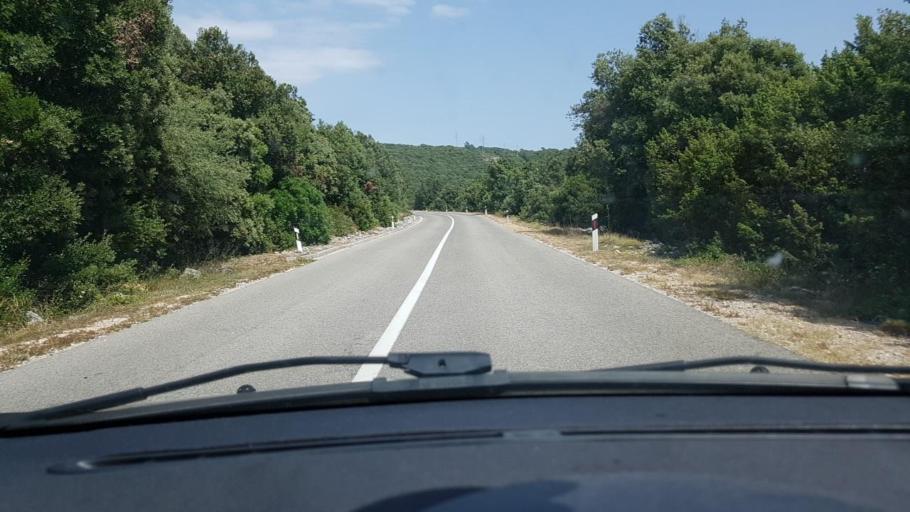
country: HR
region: Dubrovacko-Neretvanska
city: Smokvica
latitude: 42.9480
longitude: 16.9951
